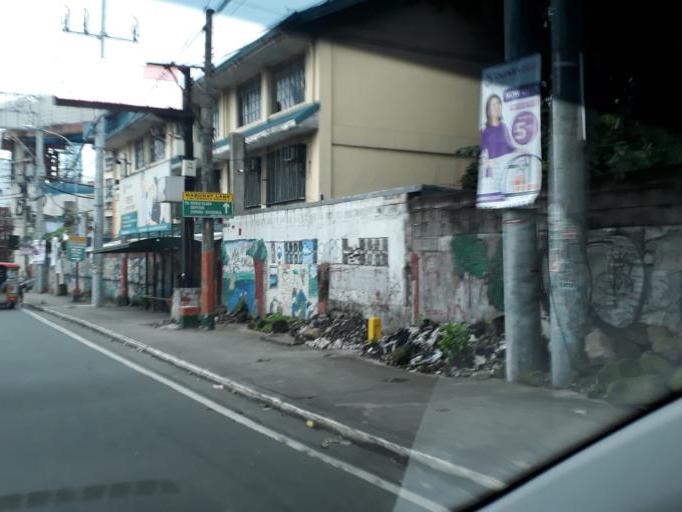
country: PH
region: Calabarzon
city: Del Monte
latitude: 14.6394
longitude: 121.0077
